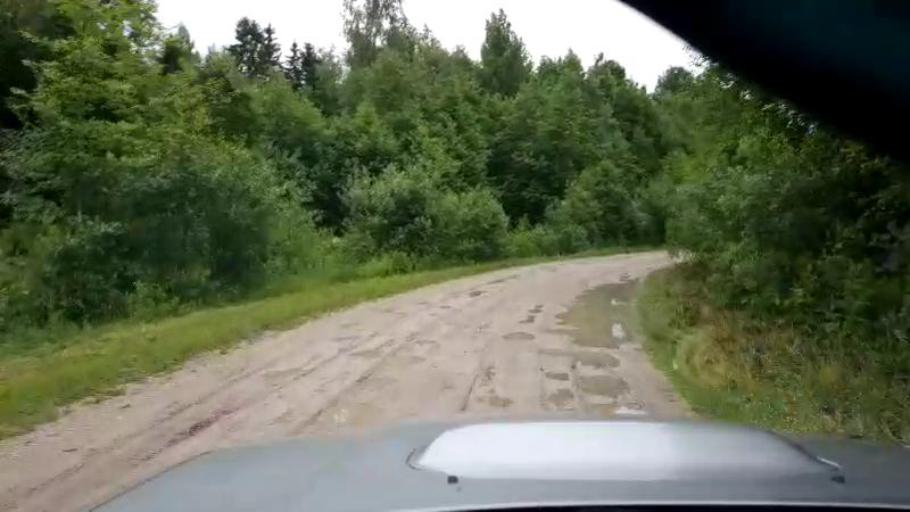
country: EE
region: Paernumaa
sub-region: Halinga vald
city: Parnu-Jaagupi
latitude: 58.5481
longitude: 24.5776
